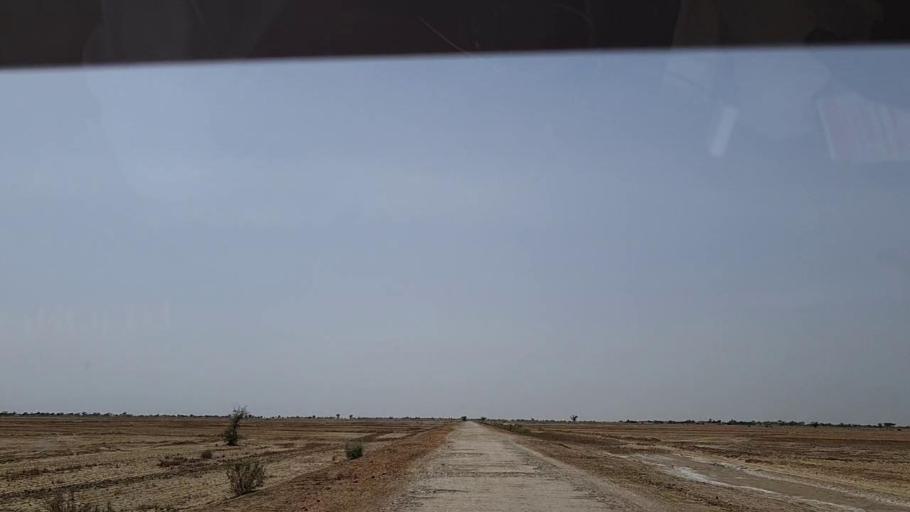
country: PK
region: Sindh
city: Johi
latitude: 26.7368
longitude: 67.6339
